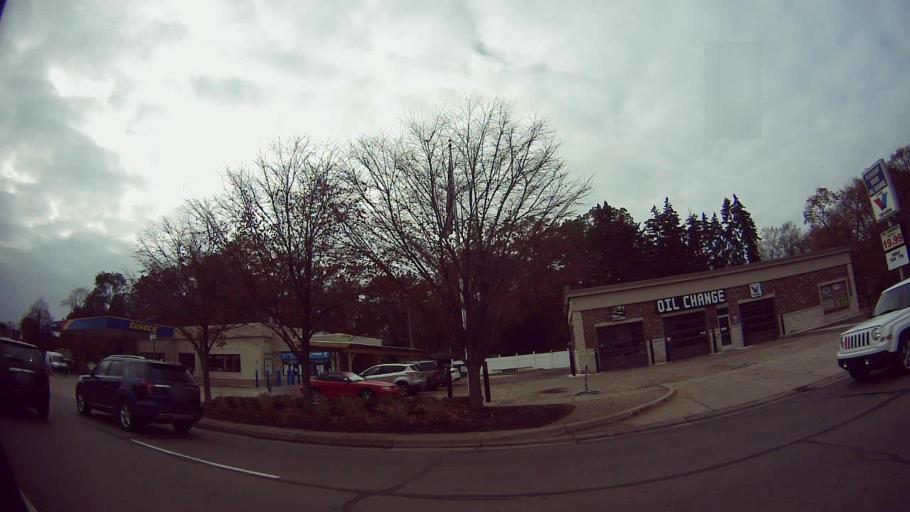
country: US
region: Michigan
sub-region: Oakland County
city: Pleasant Ridge
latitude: 42.4692
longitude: -83.1407
